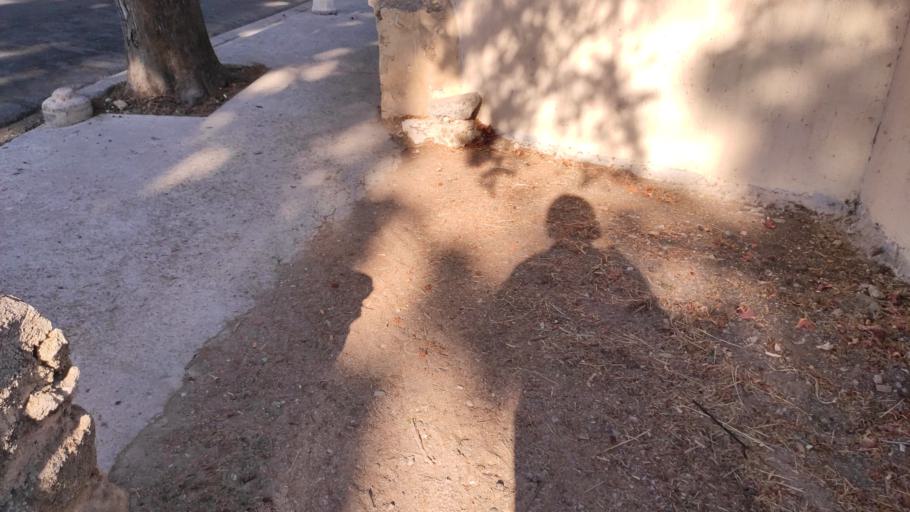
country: GR
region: South Aegean
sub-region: Nomos Dodekanisou
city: Rodos
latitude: 36.4392
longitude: 28.2287
